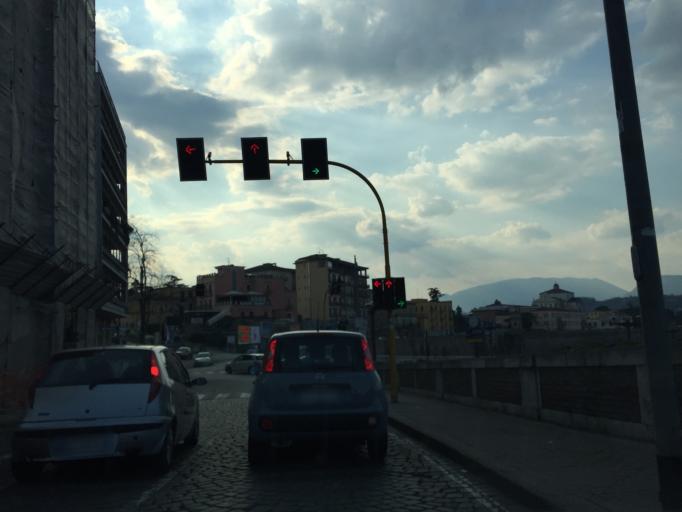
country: IT
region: Campania
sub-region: Provincia di Benevento
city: Benevento
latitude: 41.1334
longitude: 14.7742
